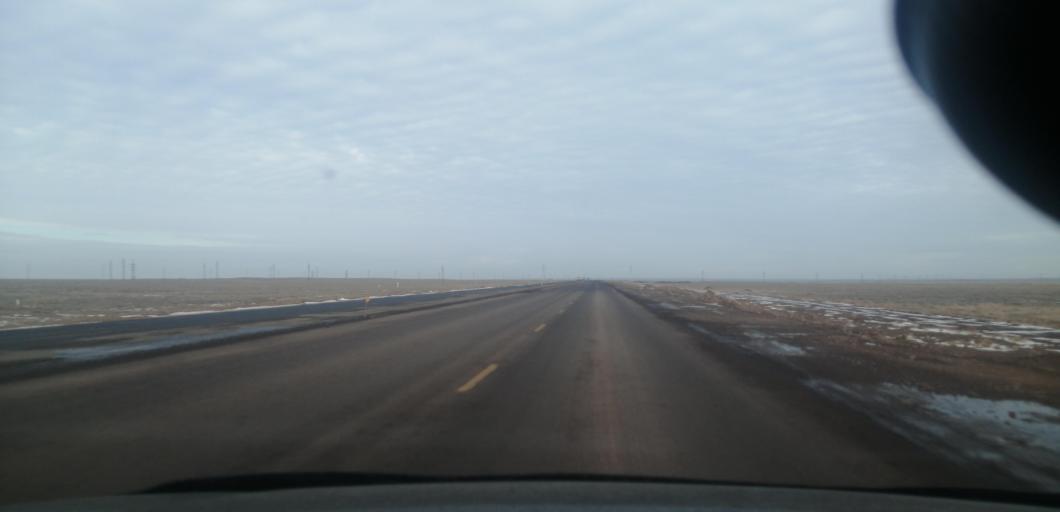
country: KZ
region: Qaraghandy
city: Balqash
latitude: 46.7730
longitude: 74.6005
